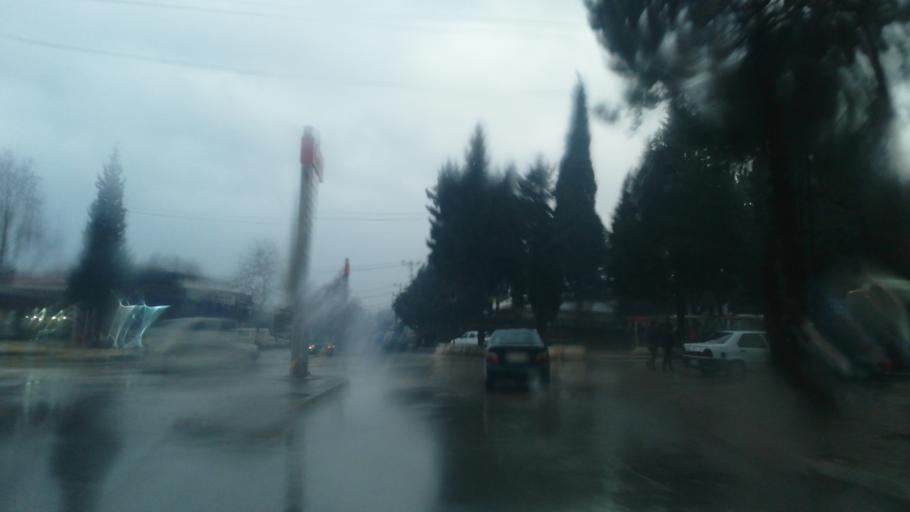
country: TR
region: Kahramanmaras
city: Kahramanmaras
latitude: 37.5625
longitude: 36.9583
